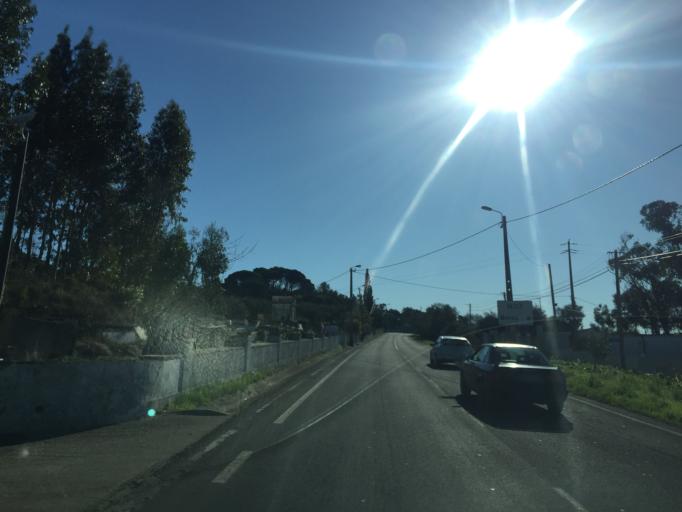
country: PT
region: Lisbon
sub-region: Sintra
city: Pero Pinheiro
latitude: 38.8378
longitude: -9.3111
